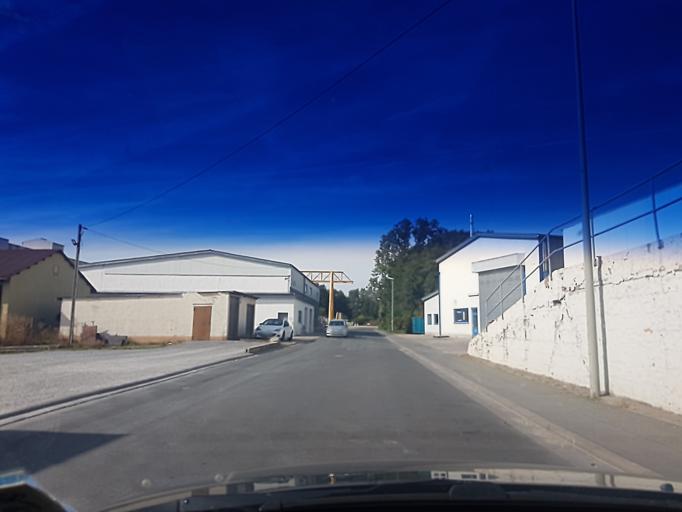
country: DE
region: Bavaria
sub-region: Upper Franconia
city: Schlusselfeld
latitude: 49.7603
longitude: 10.6142
